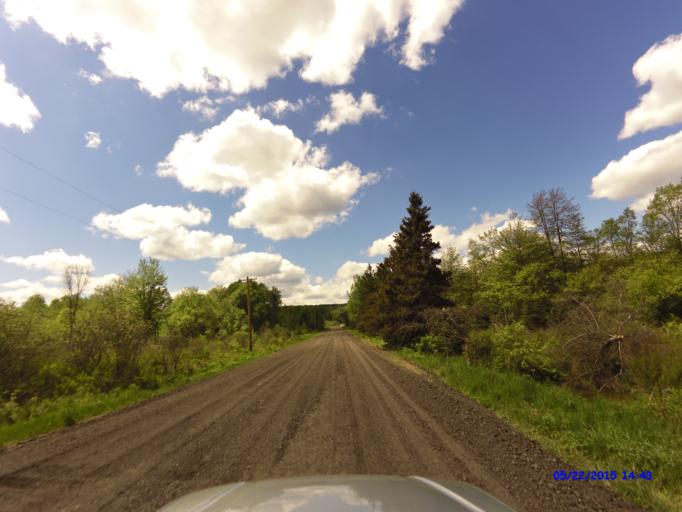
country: US
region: New York
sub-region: Cattaraugus County
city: Franklinville
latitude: 42.3534
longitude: -78.5597
